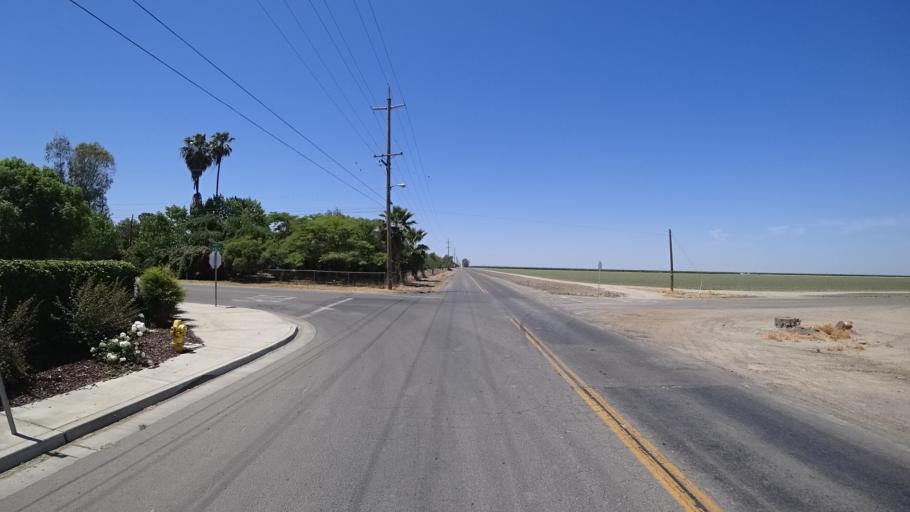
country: US
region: California
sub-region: Kings County
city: Corcoran
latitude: 36.1089
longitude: -119.5807
